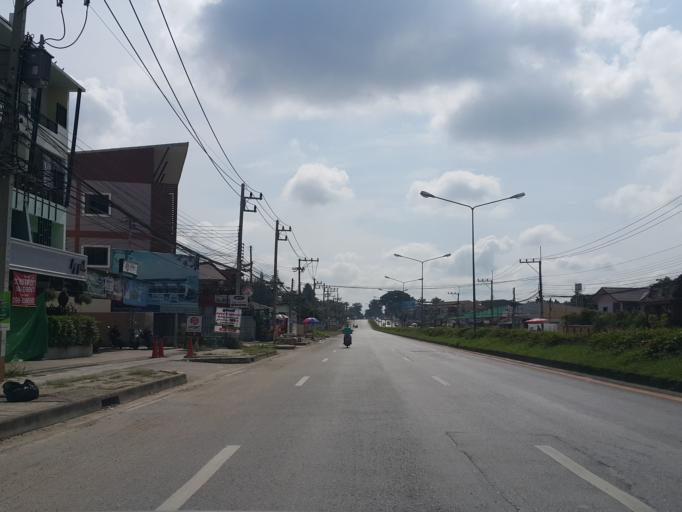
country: TH
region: Chiang Mai
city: San Sai
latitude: 18.8901
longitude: 99.0236
